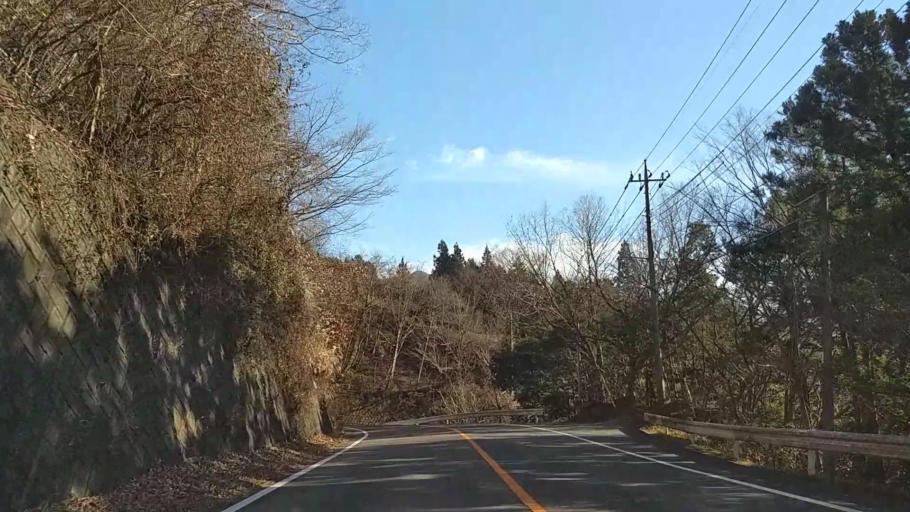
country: JP
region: Yamanashi
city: Uenohara
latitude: 35.5332
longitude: 139.0941
